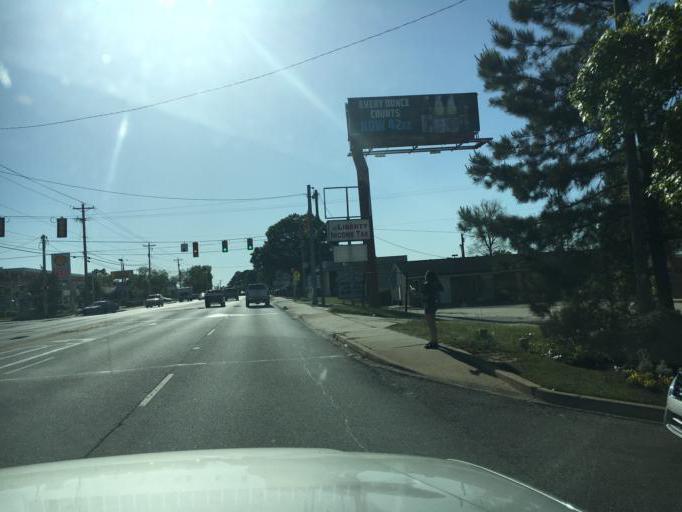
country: US
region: South Carolina
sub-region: Lexington County
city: Saint Andrews
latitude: 34.0452
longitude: -81.1255
